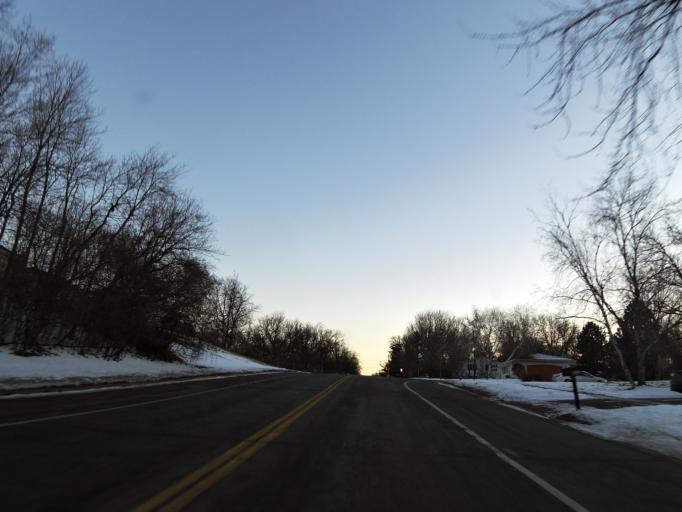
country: US
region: Minnesota
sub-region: Scott County
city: Savage
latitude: 44.8206
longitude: -93.3585
